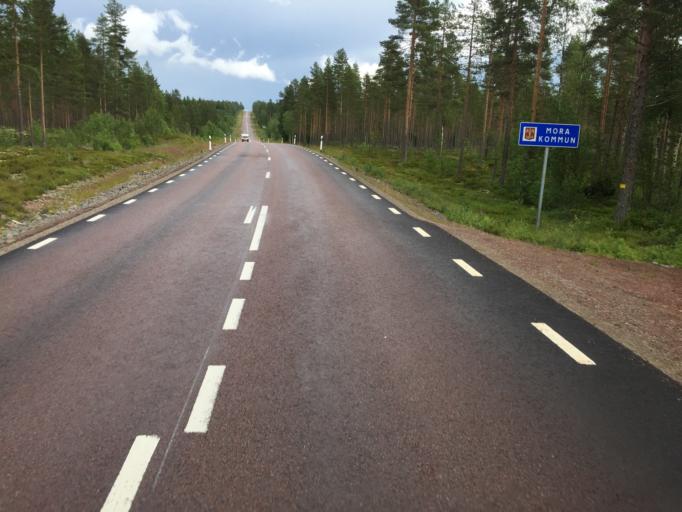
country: SE
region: Dalarna
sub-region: Malung-Saelens kommun
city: Malung
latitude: 60.8239
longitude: 13.9968
